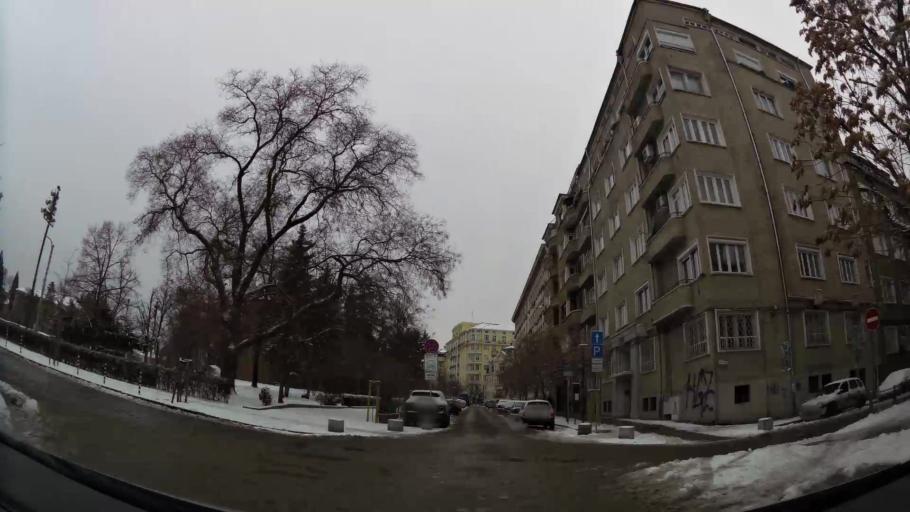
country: BG
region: Sofia-Capital
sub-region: Stolichna Obshtina
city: Sofia
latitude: 42.6968
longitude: 23.3327
